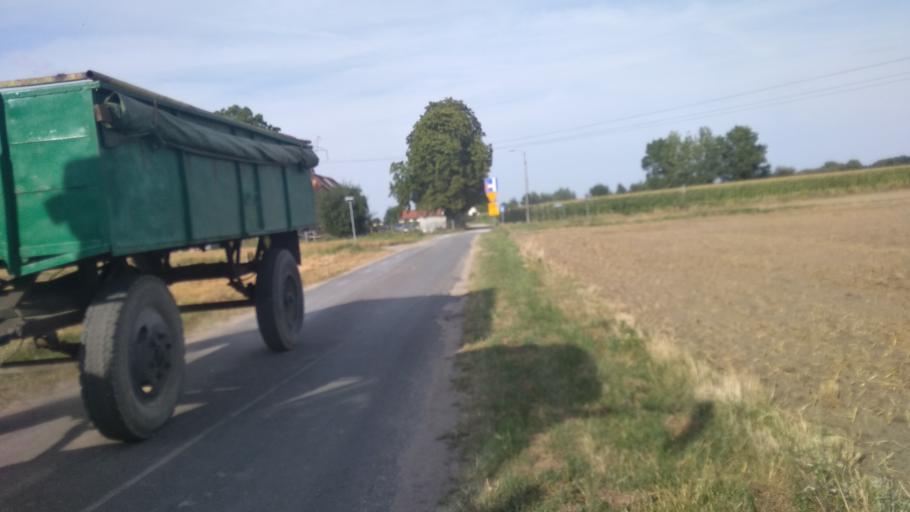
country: PL
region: Kujawsko-Pomorskie
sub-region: Powiat bydgoski
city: Osielsko
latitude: 53.2233
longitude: 18.1420
